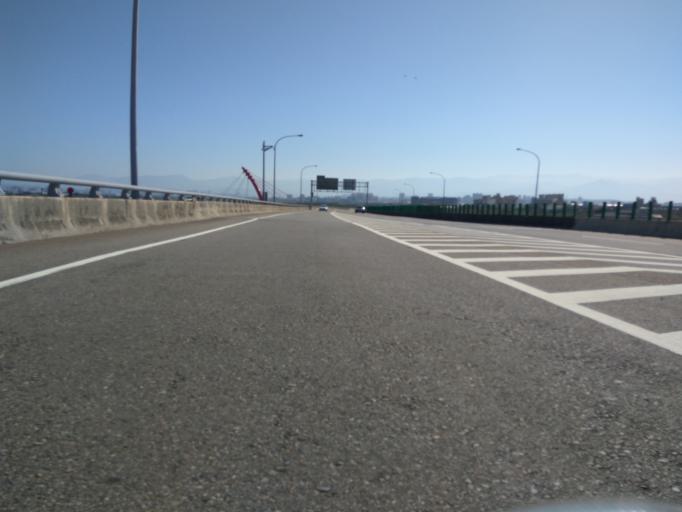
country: TW
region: Taiwan
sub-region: Hsinchu
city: Hsinchu
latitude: 24.8432
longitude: 120.9382
